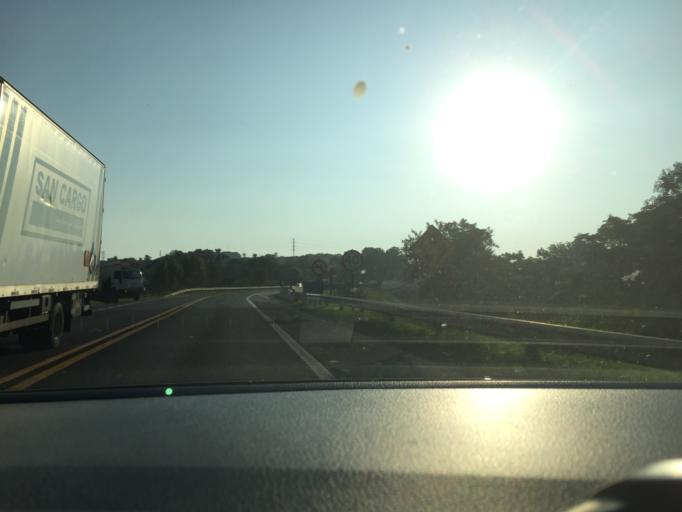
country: BR
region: Sao Paulo
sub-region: Louveira
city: Louveira
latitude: -23.0886
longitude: -46.9471
